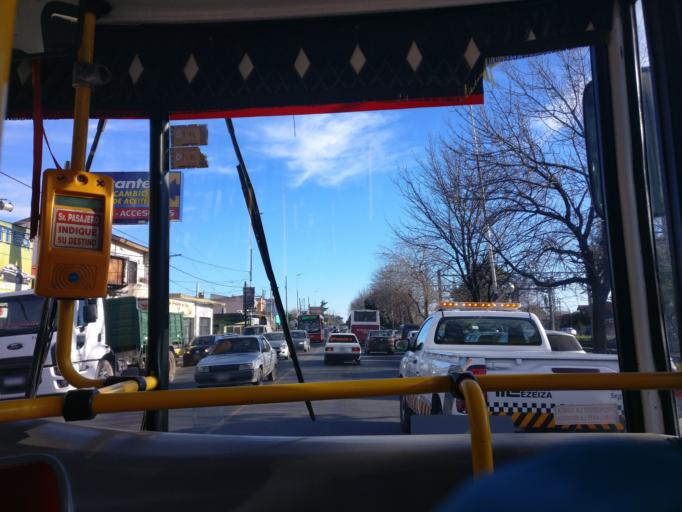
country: AR
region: Buenos Aires
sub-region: Partido de Ezeiza
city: Ezeiza
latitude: -34.8564
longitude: -58.5254
